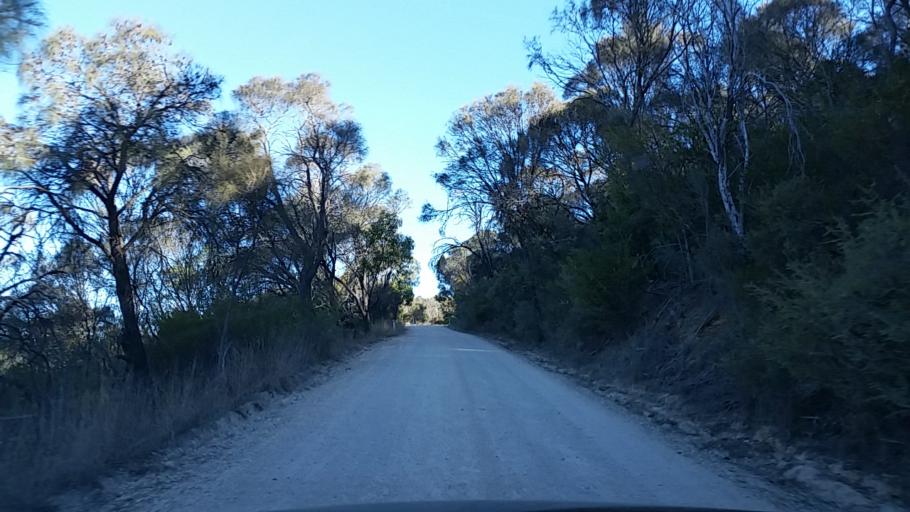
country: AU
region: South Australia
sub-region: Mount Barker
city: Nairne
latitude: -35.0651
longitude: 138.9234
